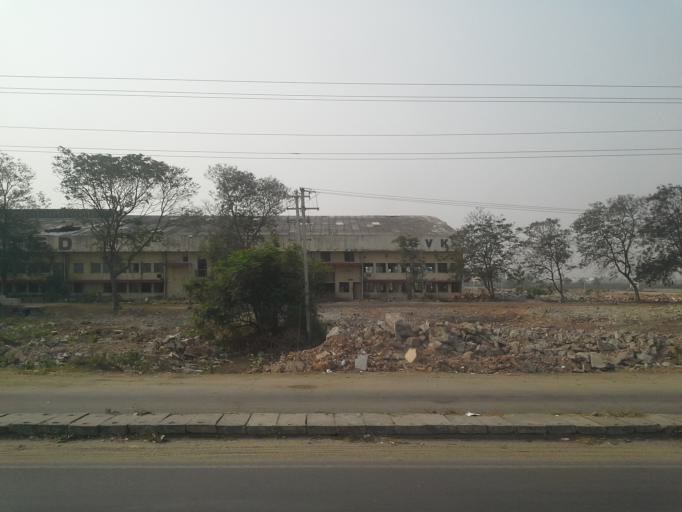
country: IN
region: Telangana
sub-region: Medak
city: Patancheru
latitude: 17.5330
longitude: 78.2524
